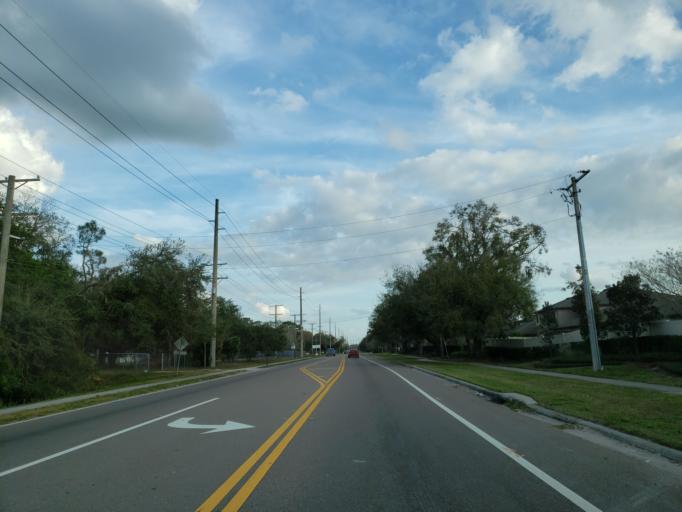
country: US
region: Florida
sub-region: Hillsborough County
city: Riverview
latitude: 27.8284
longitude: -82.3031
